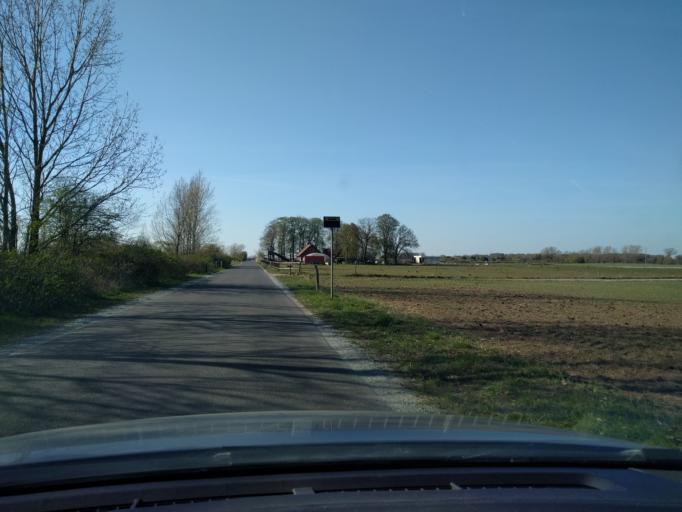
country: DK
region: South Denmark
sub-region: Kerteminde Kommune
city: Langeskov
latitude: 55.3743
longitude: 10.5853
